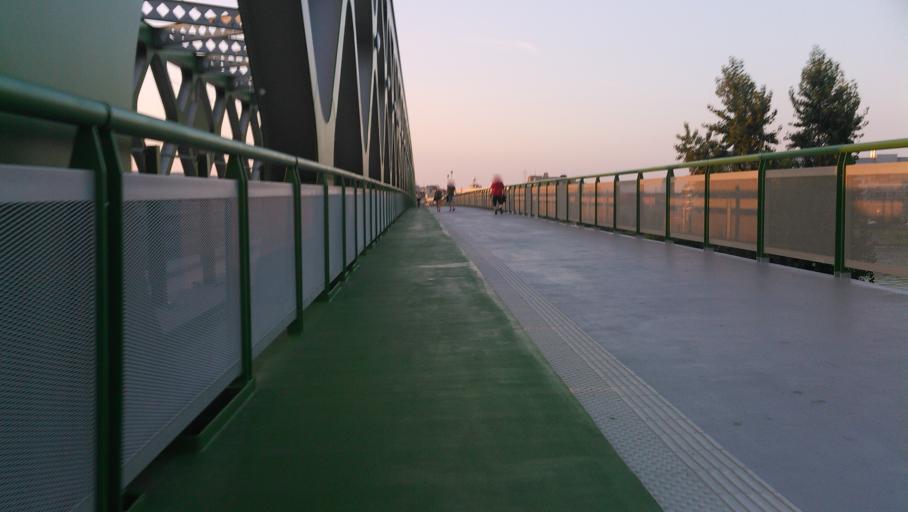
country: SK
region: Bratislavsky
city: Bratislava
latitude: 48.1364
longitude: 17.1172
